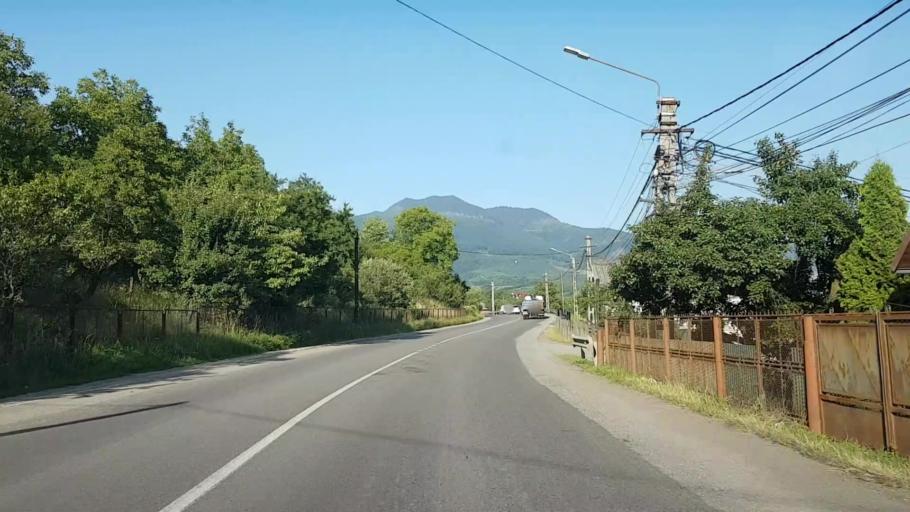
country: RO
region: Bistrita-Nasaud
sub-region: Comuna Tiha Bargaului
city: Tureac
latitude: 47.2301
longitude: 24.7868
